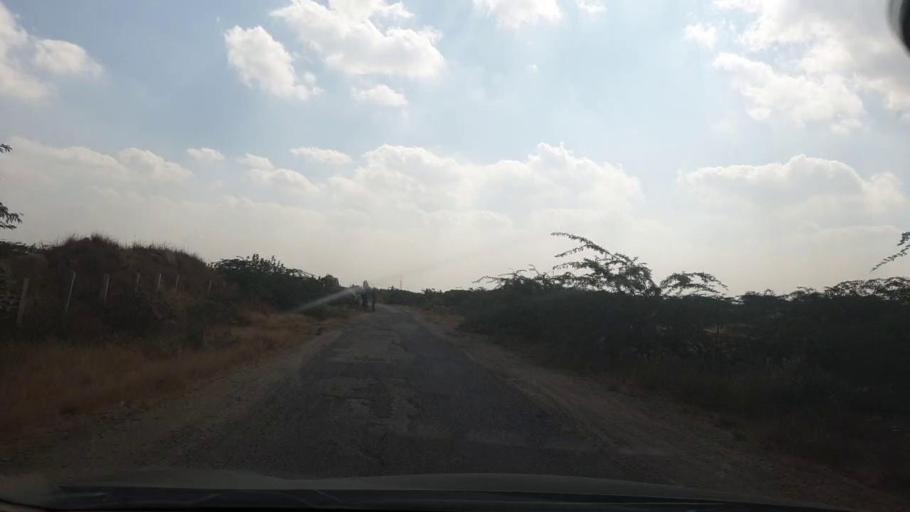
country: PK
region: Sindh
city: Malir Cantonment
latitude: 25.0244
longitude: 67.3529
